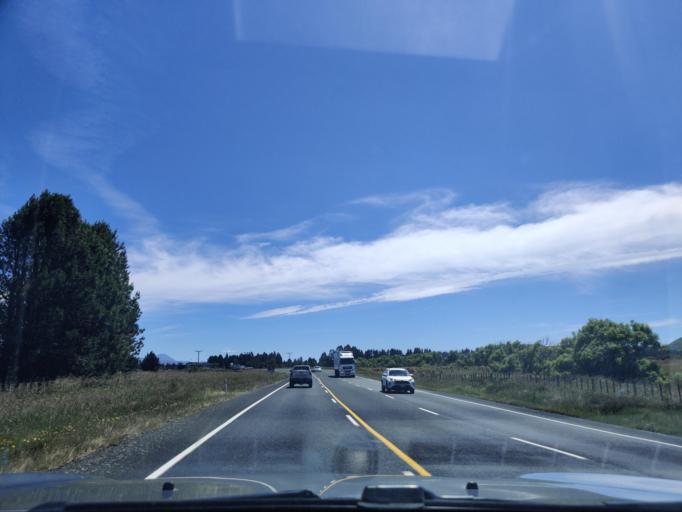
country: NZ
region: Manawatu-Wanganui
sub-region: Ruapehu District
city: Waiouru
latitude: -39.4874
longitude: 175.6696
